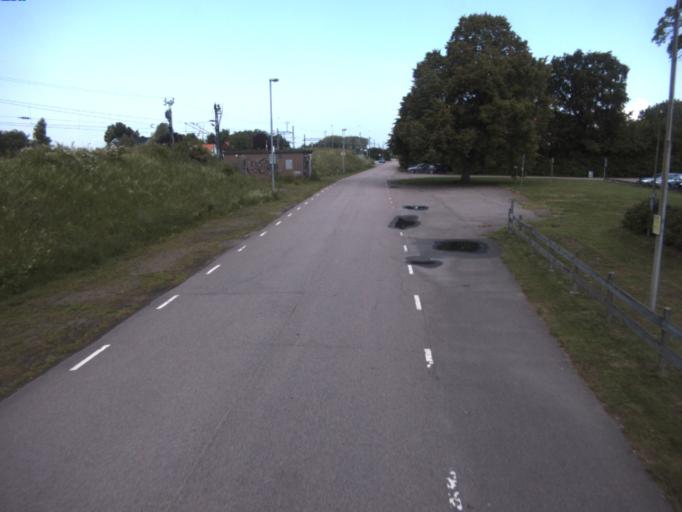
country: SE
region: Skane
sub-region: Angelholms Kommun
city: Strovelstorp
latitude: 56.1429
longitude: 12.7789
